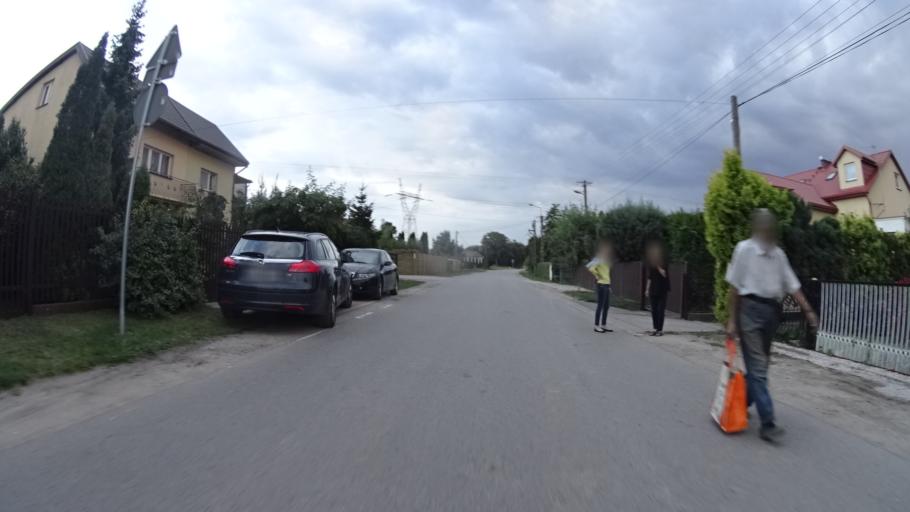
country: PL
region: Masovian Voivodeship
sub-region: Powiat warszawski zachodni
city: Stare Babice
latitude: 52.2343
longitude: 20.8256
